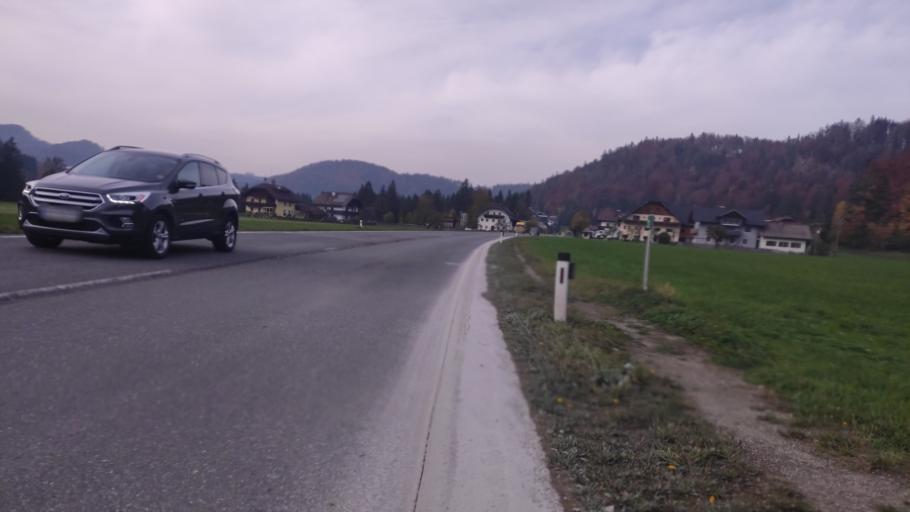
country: AT
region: Salzburg
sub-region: Politischer Bezirk Salzburg-Umgebung
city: Ebenau
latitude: 47.7833
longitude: 13.1791
